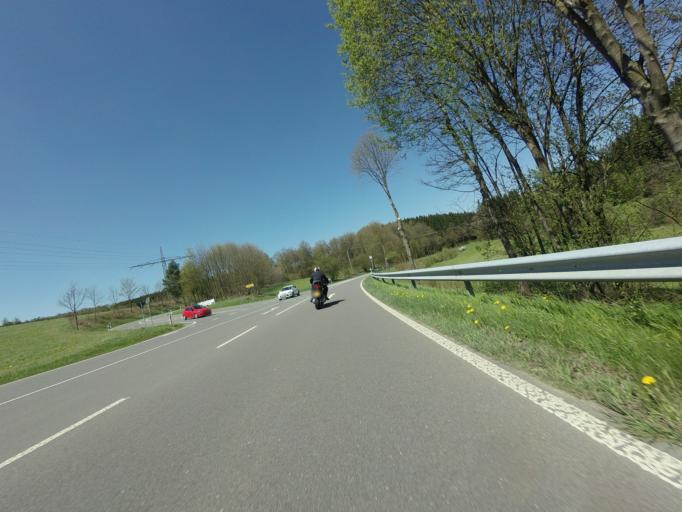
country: DE
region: North Rhine-Westphalia
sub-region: Regierungsbezirk Arnsberg
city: Olpe
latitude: 51.0115
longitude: 7.9067
